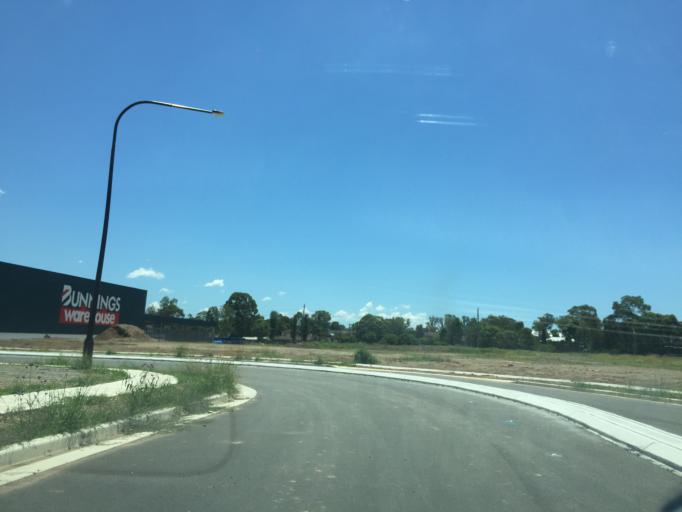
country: AU
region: New South Wales
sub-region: Blacktown
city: Mount Druitt
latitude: -33.7805
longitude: 150.8119
